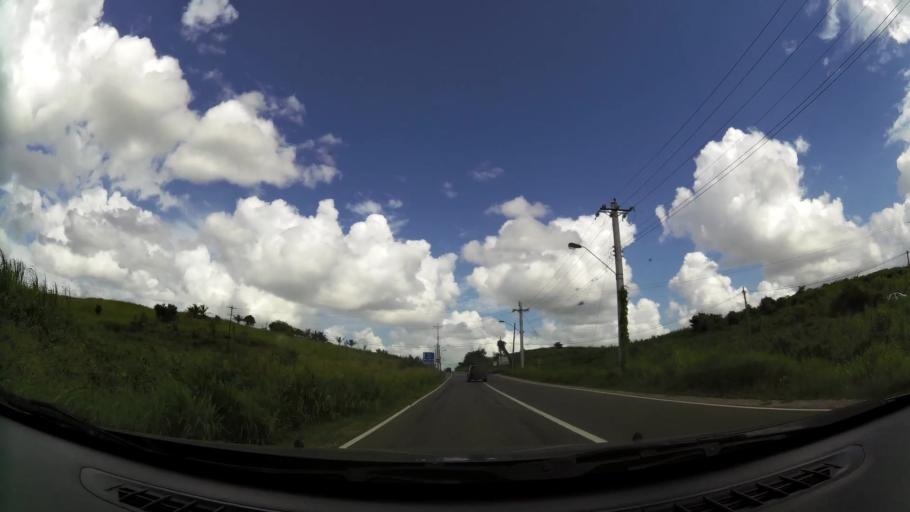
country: TT
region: Penal/Debe
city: Debe
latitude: 10.2303
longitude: -61.4871
